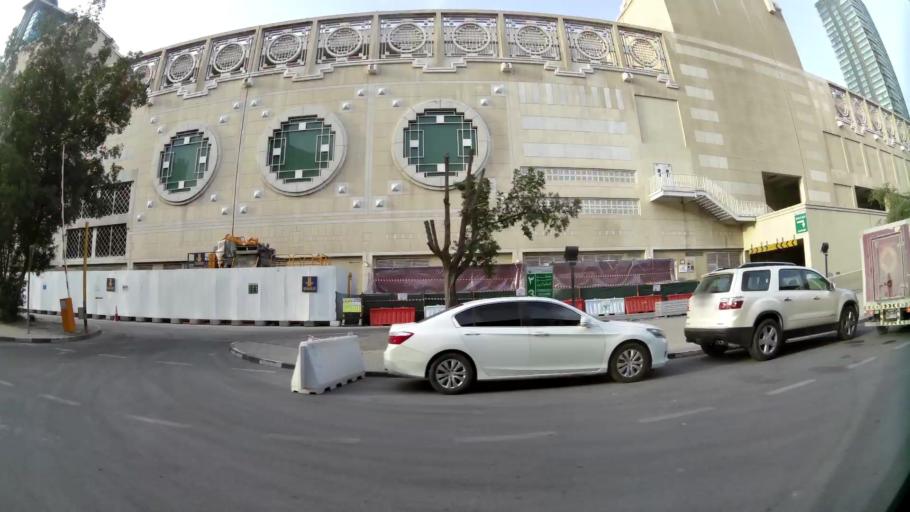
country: QA
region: Baladiyat ad Dawhah
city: Doha
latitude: 25.3238
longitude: 51.5308
